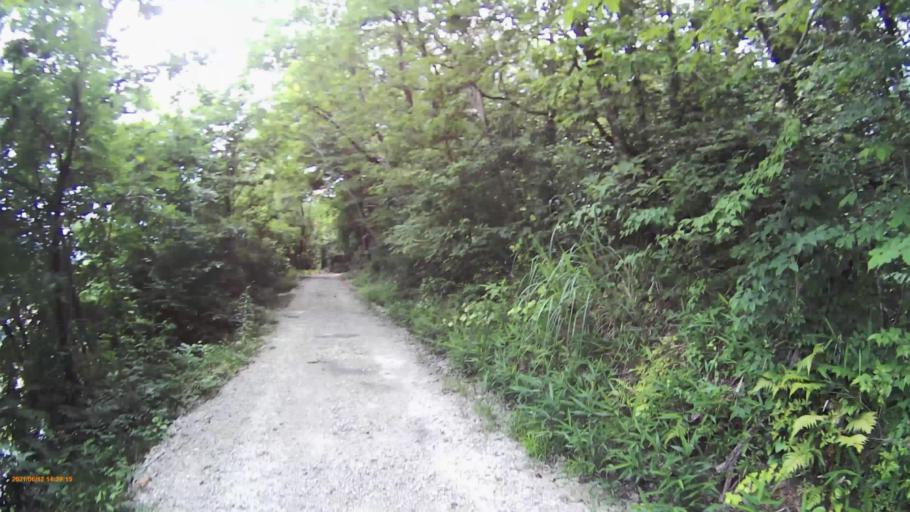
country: JP
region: Gifu
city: Nakatsugawa
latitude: 35.4463
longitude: 137.3761
